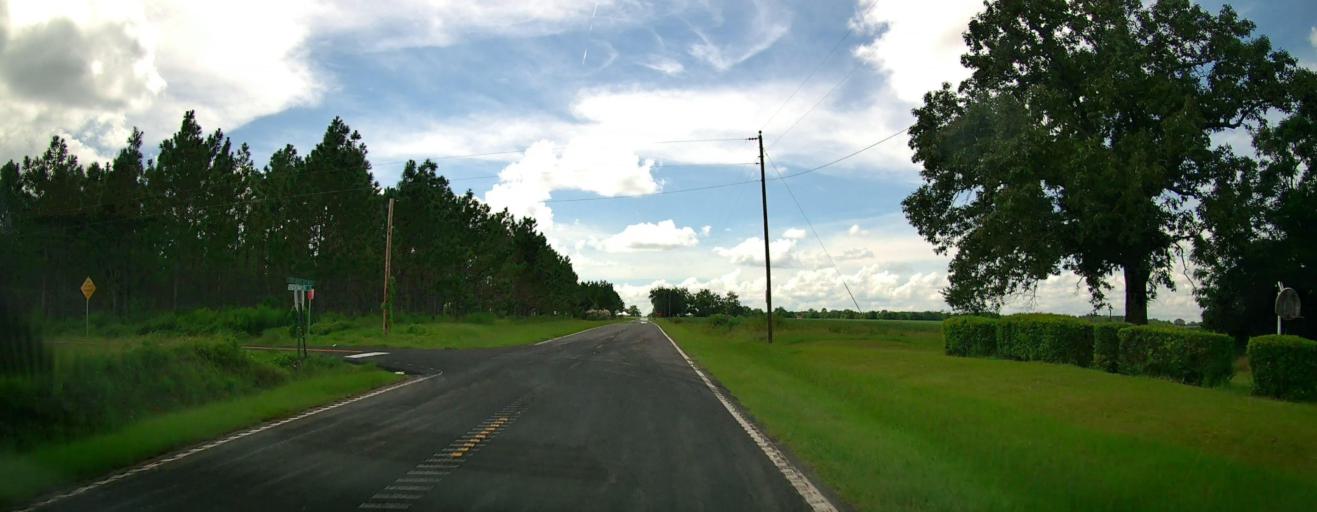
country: US
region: Georgia
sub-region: Taylor County
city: Reynolds
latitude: 32.4402
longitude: -84.1278
